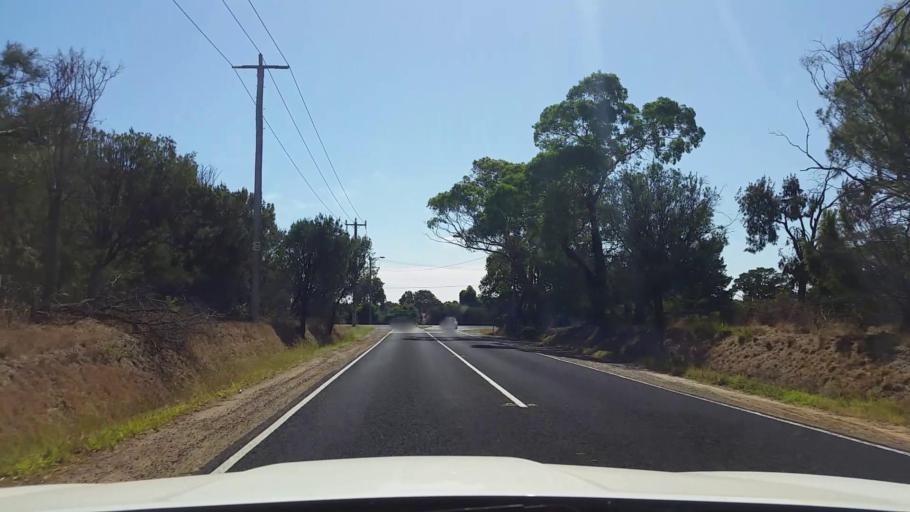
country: AU
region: Victoria
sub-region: Mornington Peninsula
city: Baxter
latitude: -38.2059
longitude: 145.1586
